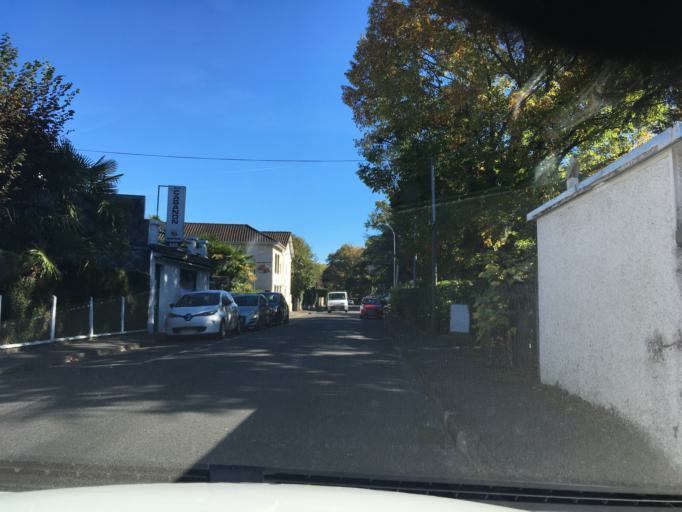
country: FR
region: Aquitaine
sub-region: Departement des Pyrenees-Atlantiques
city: Pau
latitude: 43.3135
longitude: -0.3714
